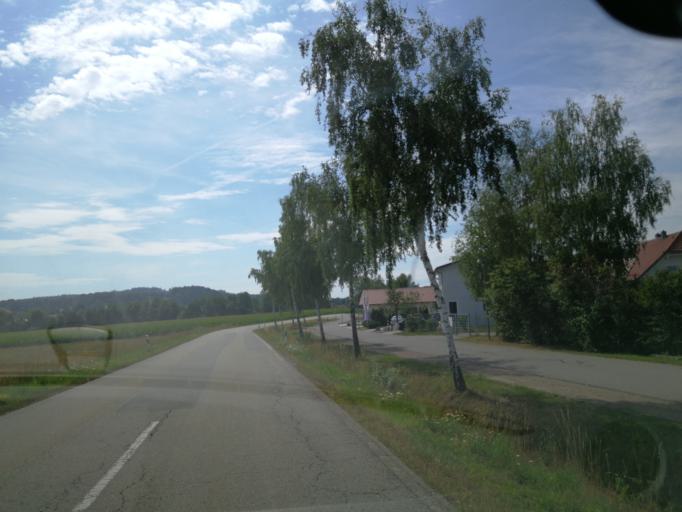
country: DE
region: Bavaria
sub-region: Lower Bavaria
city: Wiesenfelden
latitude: 49.0467
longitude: 12.5325
